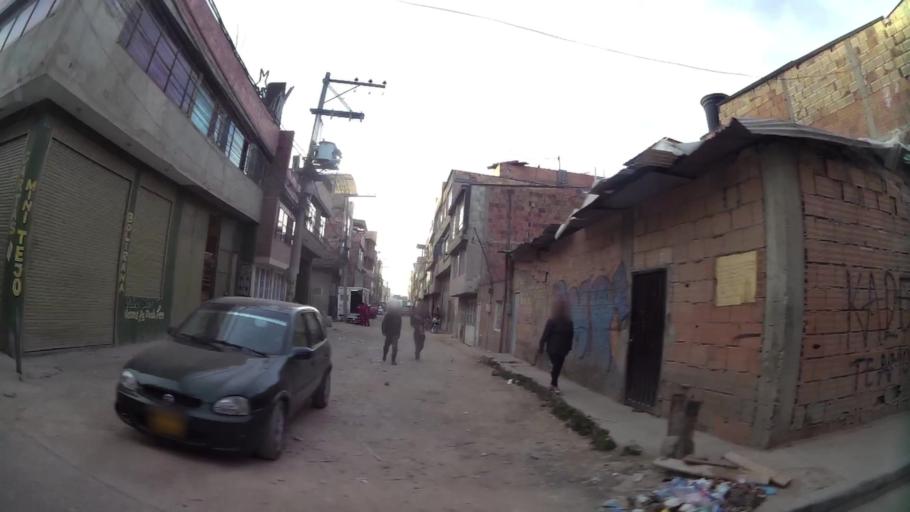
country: CO
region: Cundinamarca
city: Soacha
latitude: 4.6299
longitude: -74.1658
